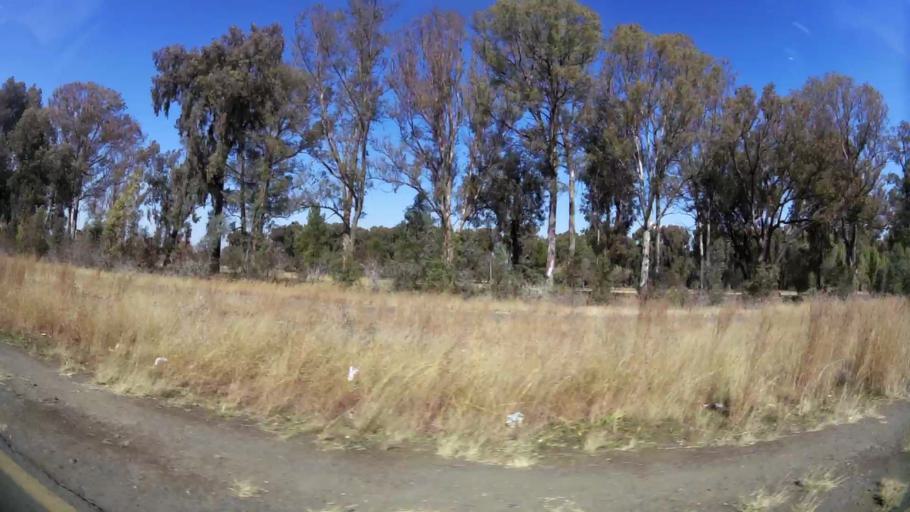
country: ZA
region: Orange Free State
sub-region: Mangaung Metropolitan Municipality
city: Bloemfontein
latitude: -29.1161
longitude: 26.2535
